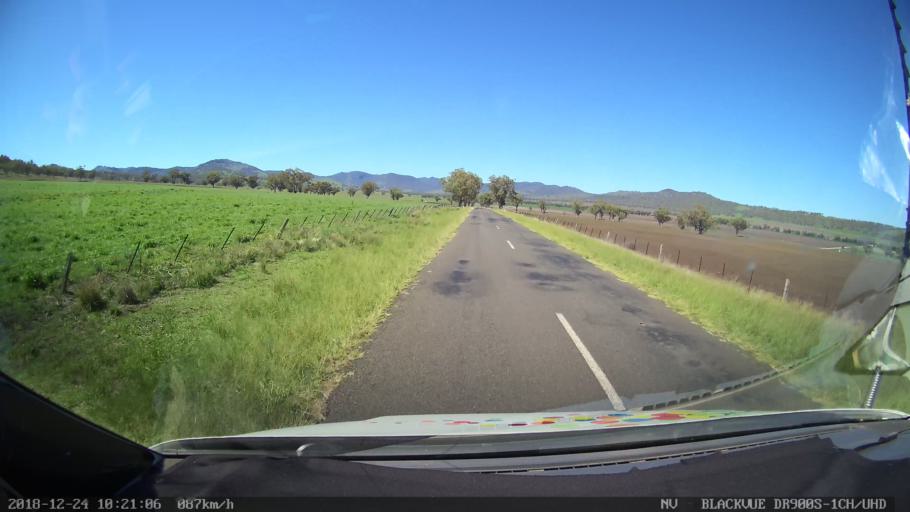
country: AU
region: New South Wales
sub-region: Liverpool Plains
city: Quirindi
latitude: -31.7483
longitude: 150.5530
